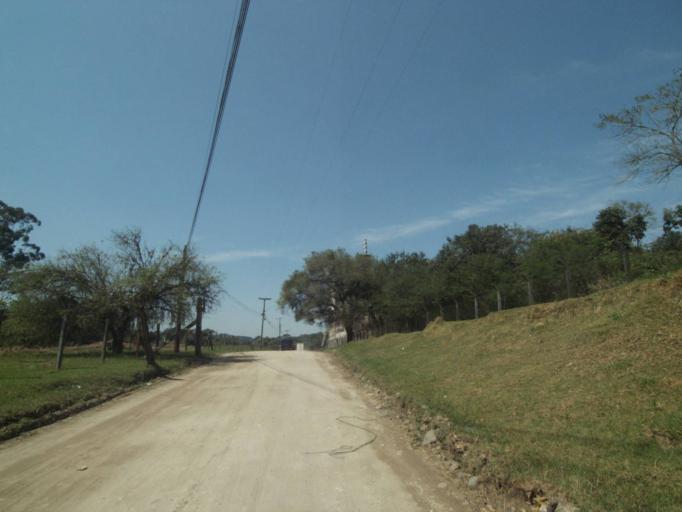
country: BR
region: Parana
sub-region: Paranagua
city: Paranagua
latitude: -25.5617
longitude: -48.6213
